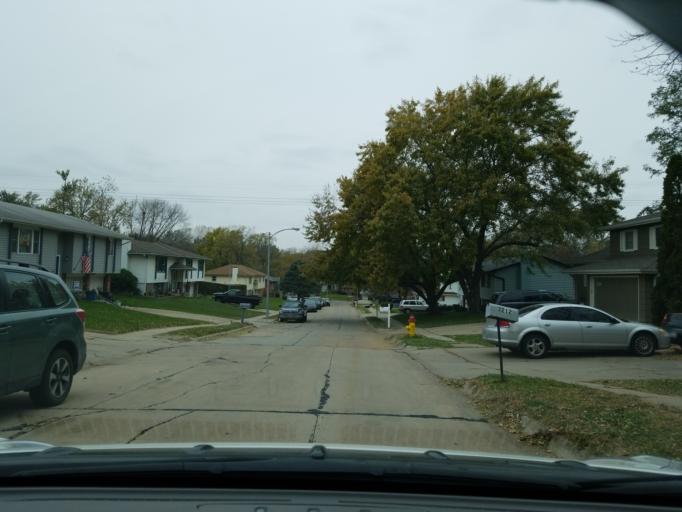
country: US
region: Nebraska
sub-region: Sarpy County
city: Offutt Air Force Base
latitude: 41.1340
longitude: -95.9608
